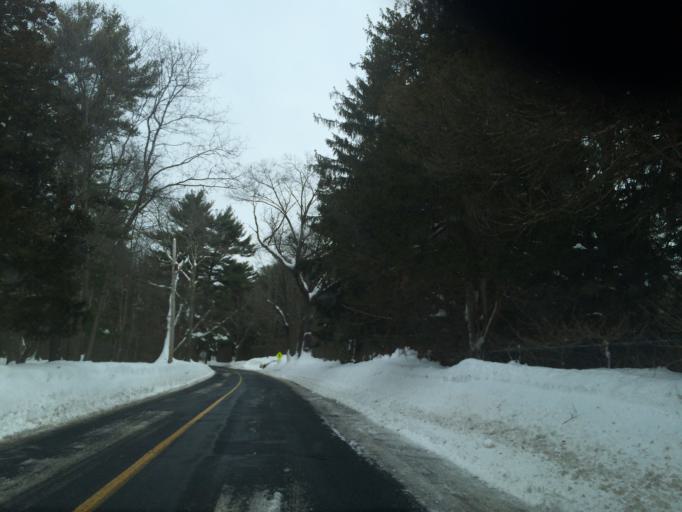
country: US
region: Massachusetts
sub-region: Middlesex County
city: Weston
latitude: 42.3514
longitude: -71.2982
